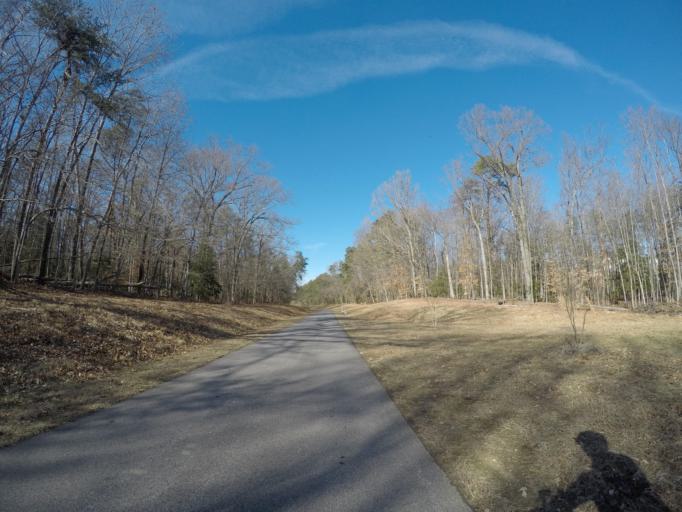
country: US
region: Maryland
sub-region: Charles County
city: Saint Charles
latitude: 38.5939
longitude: -76.9493
